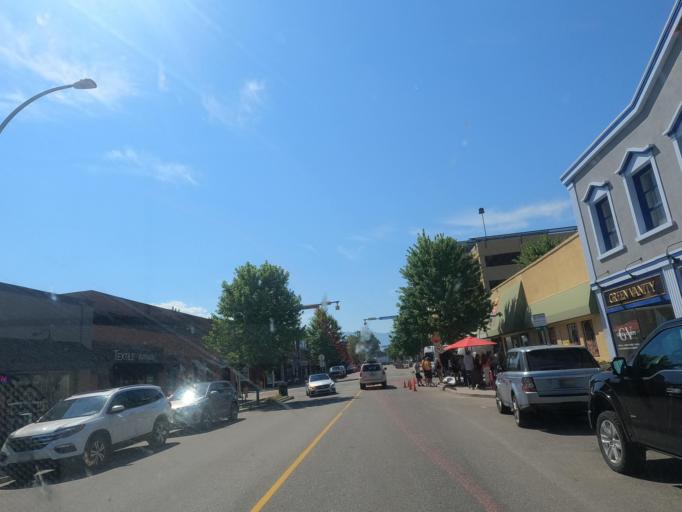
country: CA
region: British Columbia
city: Kelowna
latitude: 49.8857
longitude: -119.4951
